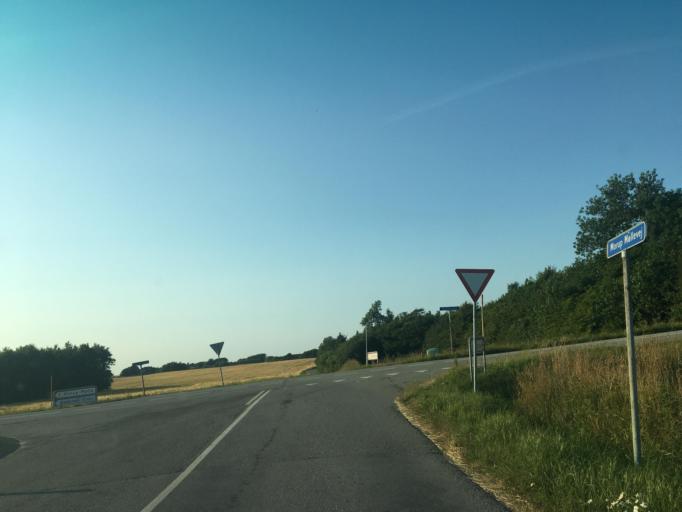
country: DK
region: North Denmark
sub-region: Thisted Kommune
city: Hurup
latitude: 56.8153
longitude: 8.4000
